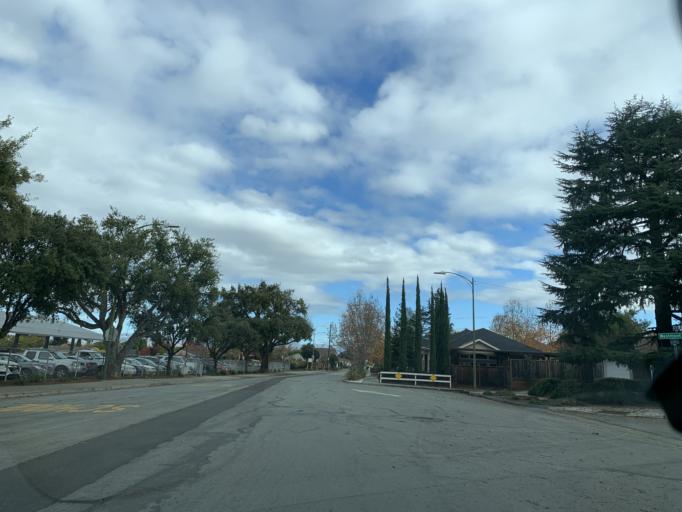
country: US
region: California
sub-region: Santa Clara County
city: Monte Sereno
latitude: 37.2708
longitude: -121.9829
